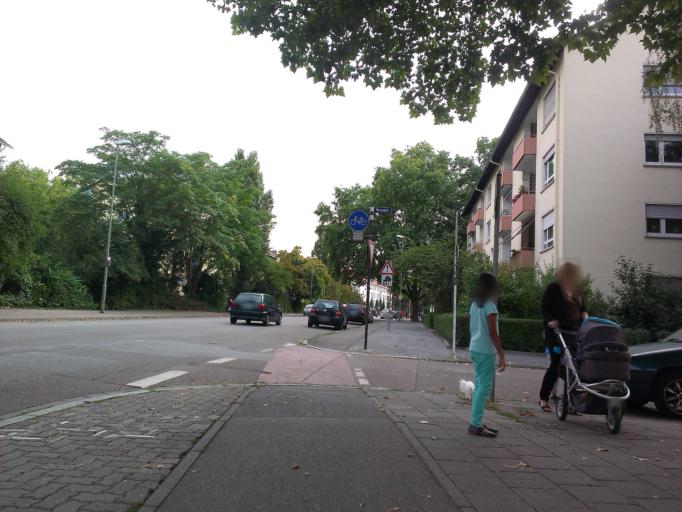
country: DE
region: Rheinland-Pfalz
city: Ludwigshafen am Rhein
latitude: 49.4715
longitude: 8.4481
